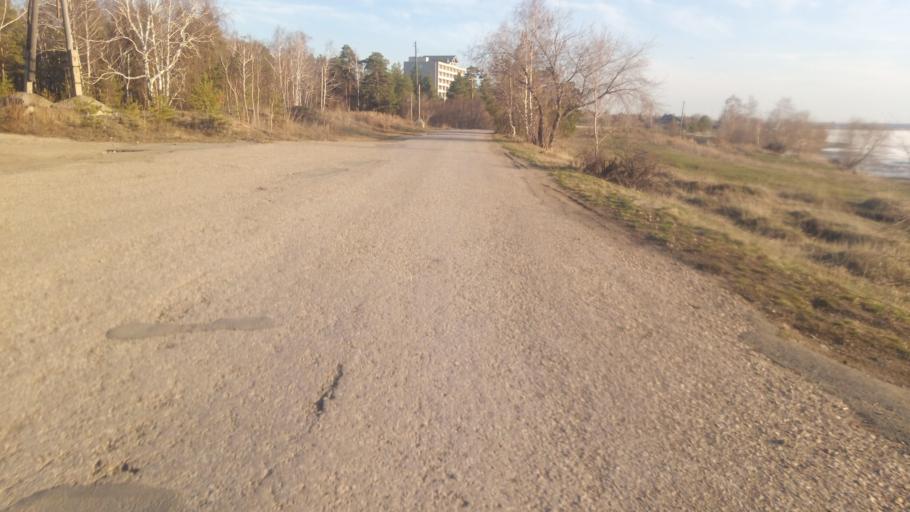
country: RU
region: Chelyabinsk
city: Novosineglazovskiy
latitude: 55.1272
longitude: 61.3284
